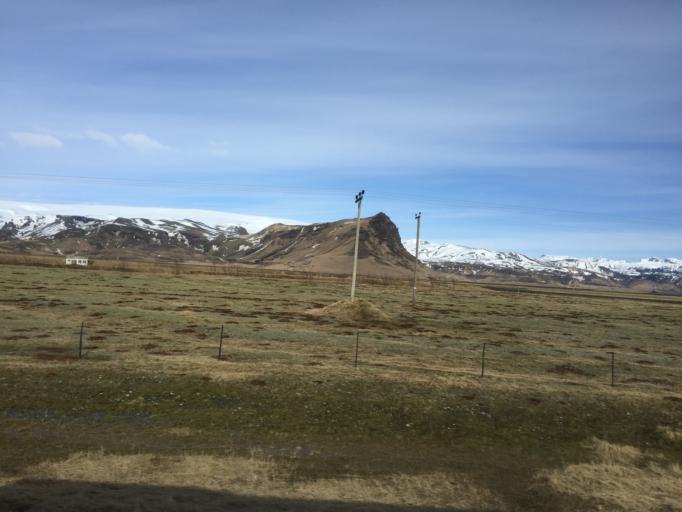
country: IS
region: South
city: Vestmannaeyjar
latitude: 63.4716
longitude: -19.2541
